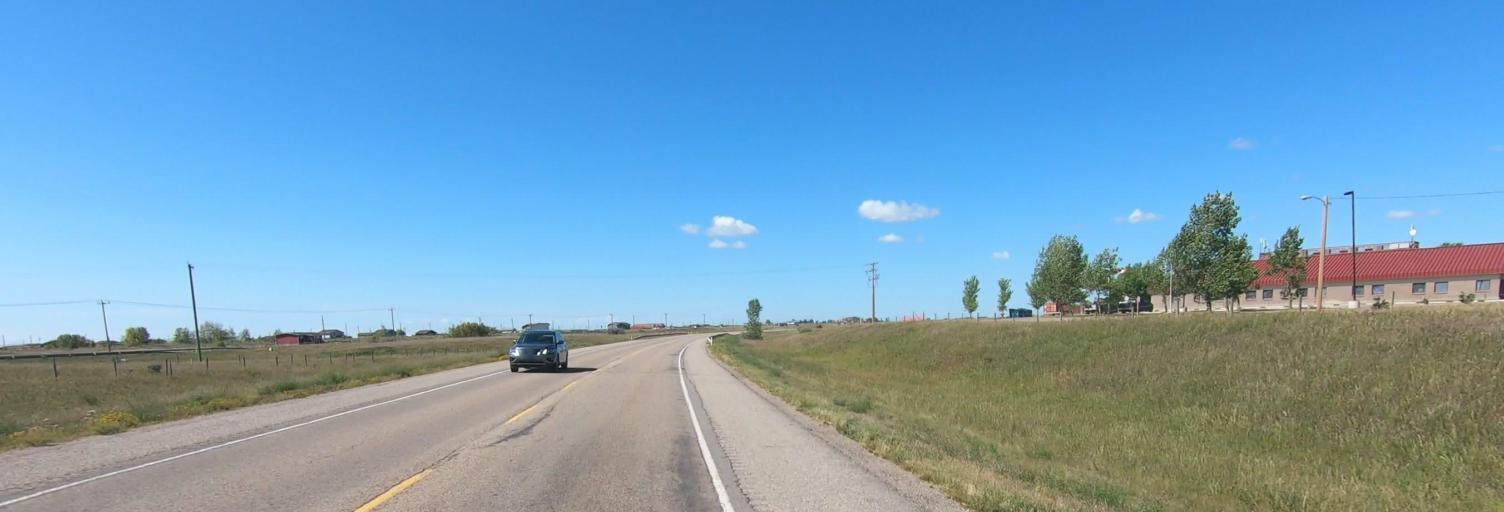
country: CA
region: Alberta
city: Strathmore
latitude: 50.8501
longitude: -113.0280
